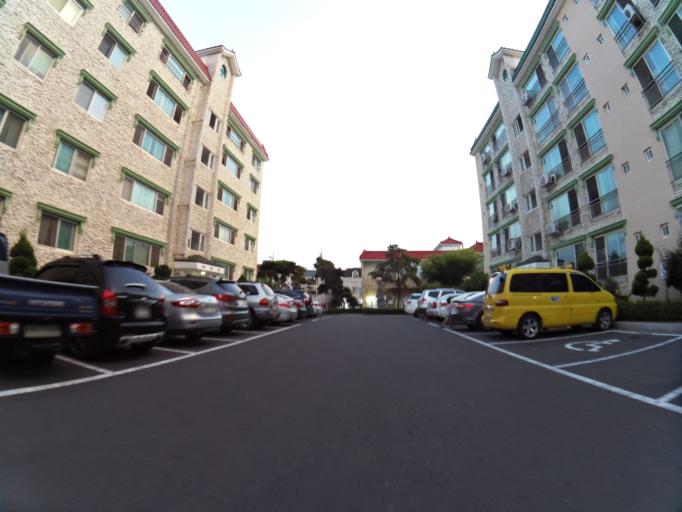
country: KR
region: Gyeongsangbuk-do
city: Gyeongsan-si
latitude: 35.8417
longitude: 128.7547
